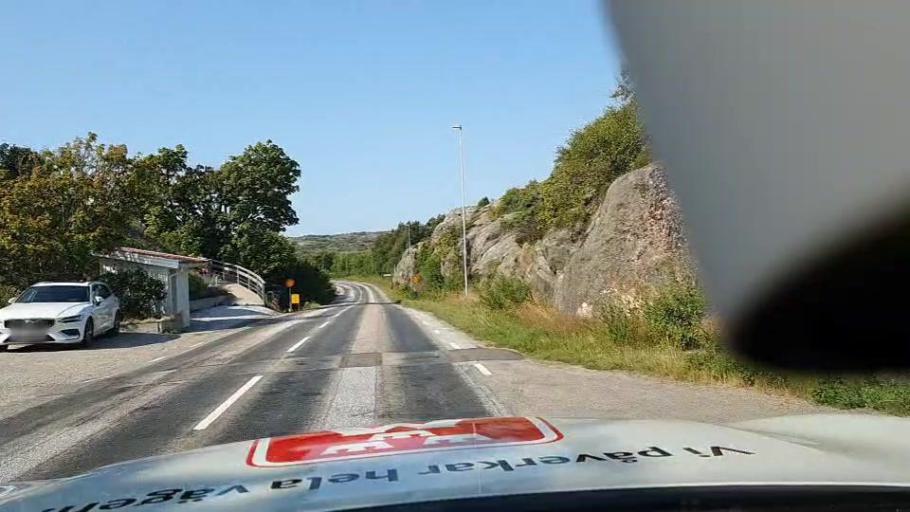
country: SE
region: Vaestra Goetaland
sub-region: Tjorns Kommun
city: Skaerhamn
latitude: 58.1116
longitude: 11.4681
